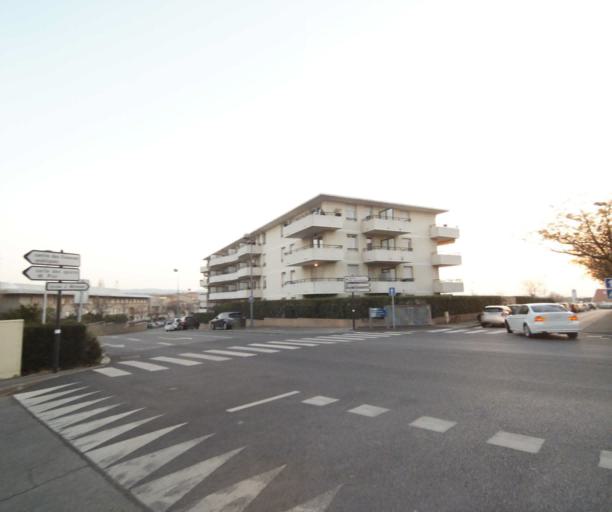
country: FR
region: Provence-Alpes-Cote d'Azur
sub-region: Departement des Bouches-du-Rhone
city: Saint-Victoret
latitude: 43.4264
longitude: 5.2723
